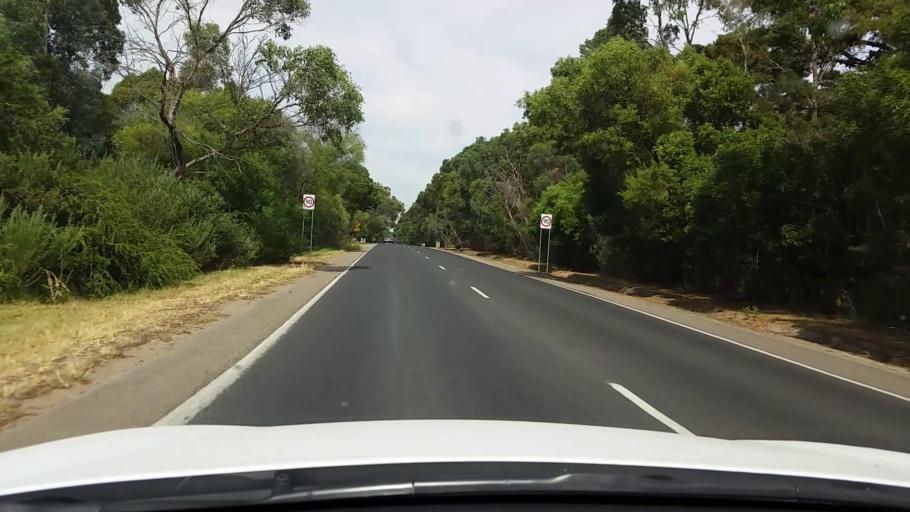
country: AU
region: Victoria
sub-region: Mornington Peninsula
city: Crib Point
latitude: -38.3457
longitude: 145.1666
